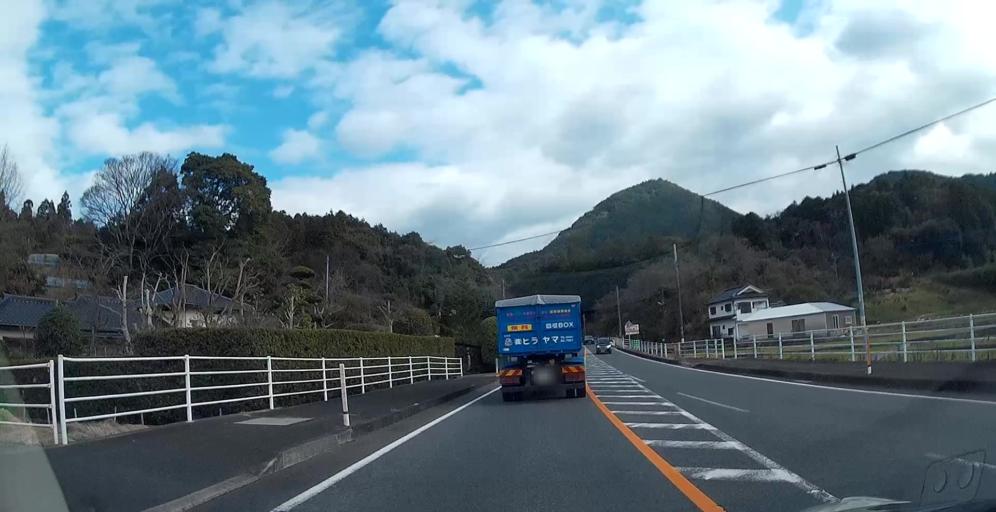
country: JP
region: Kumamoto
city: Minamata
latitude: 32.2258
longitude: 130.4388
